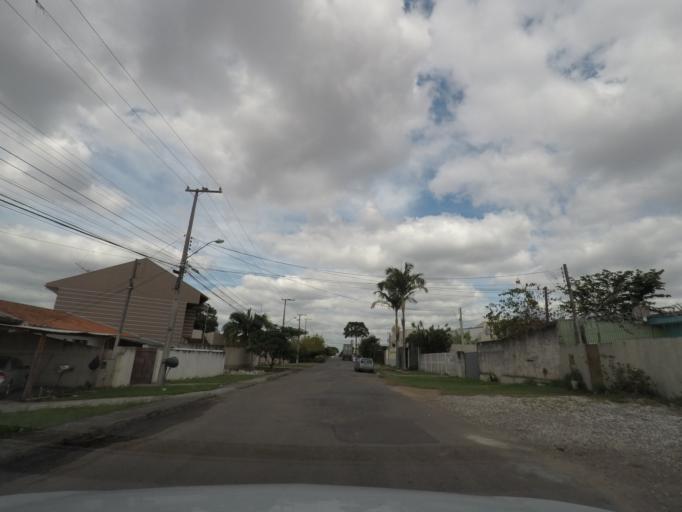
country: BR
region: Parana
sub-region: Sao Jose Dos Pinhais
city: Sao Jose dos Pinhais
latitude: -25.4909
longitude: -49.2373
